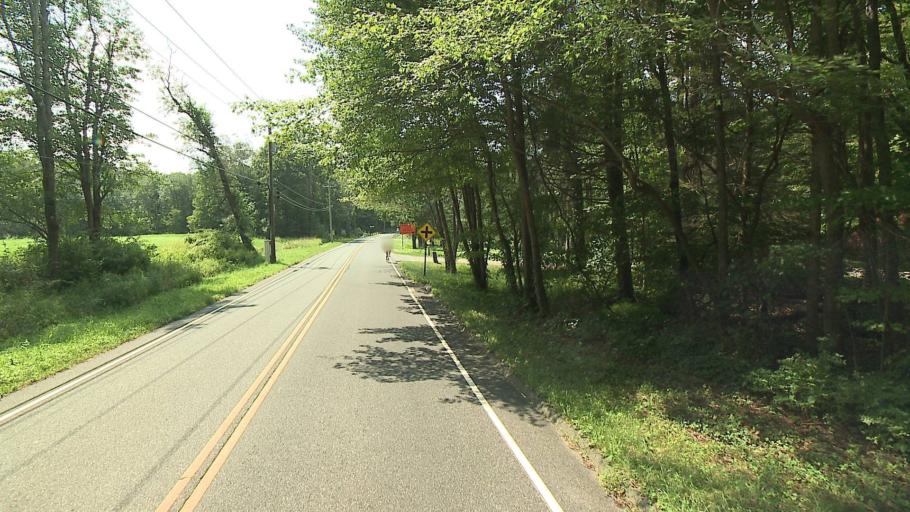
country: US
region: Connecticut
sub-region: Litchfield County
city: New Preston
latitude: 41.6571
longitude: -73.2795
